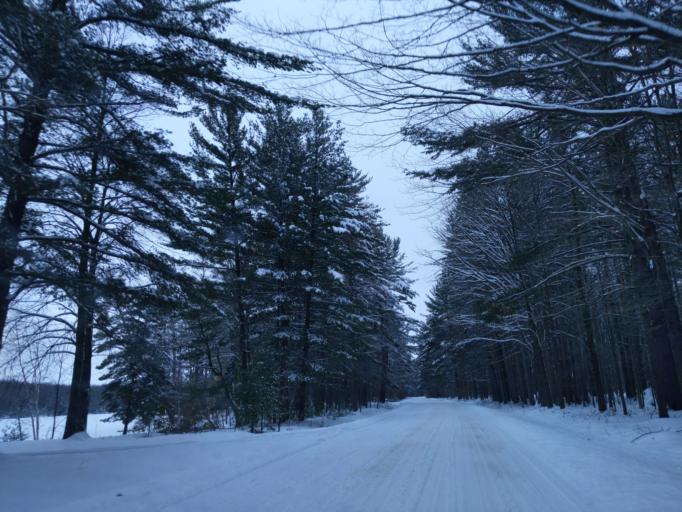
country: US
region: Wisconsin
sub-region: Marathon County
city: Marathon
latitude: 44.7664
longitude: -89.8694
